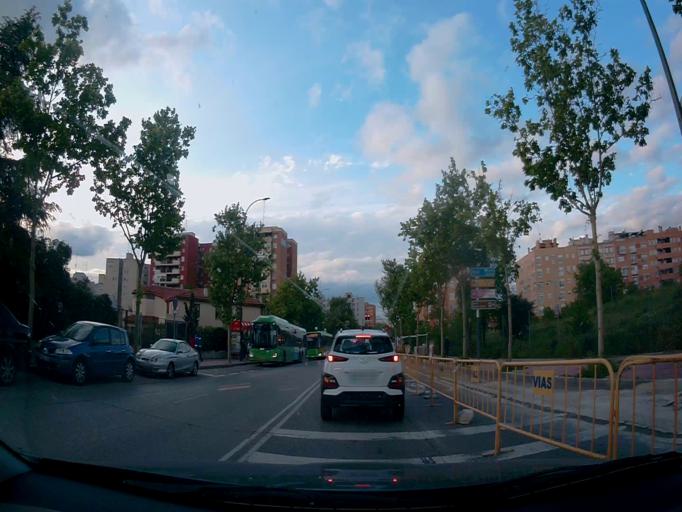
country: ES
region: Madrid
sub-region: Provincia de Madrid
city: Mostoles
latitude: 40.3249
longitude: -3.8826
